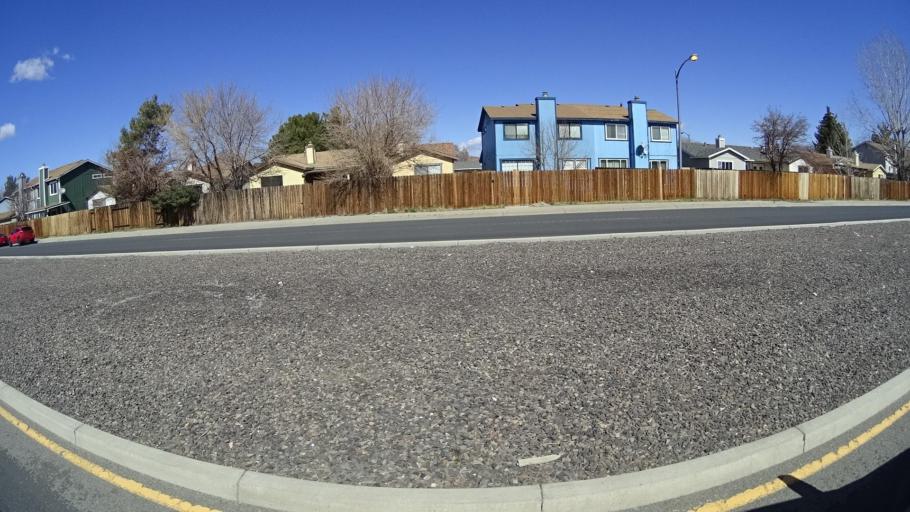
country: US
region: Nevada
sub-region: Washoe County
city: Lemmon Valley
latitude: 39.6418
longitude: -119.8777
